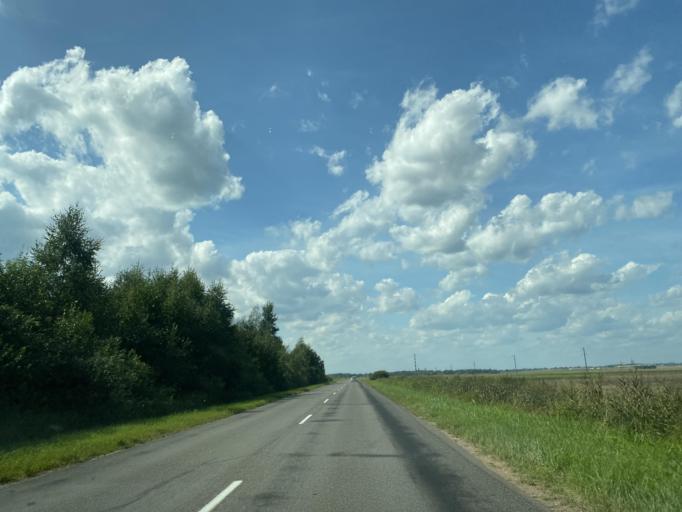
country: BY
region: Minsk
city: Horad Zhodzina
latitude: 54.0704
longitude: 28.4149
